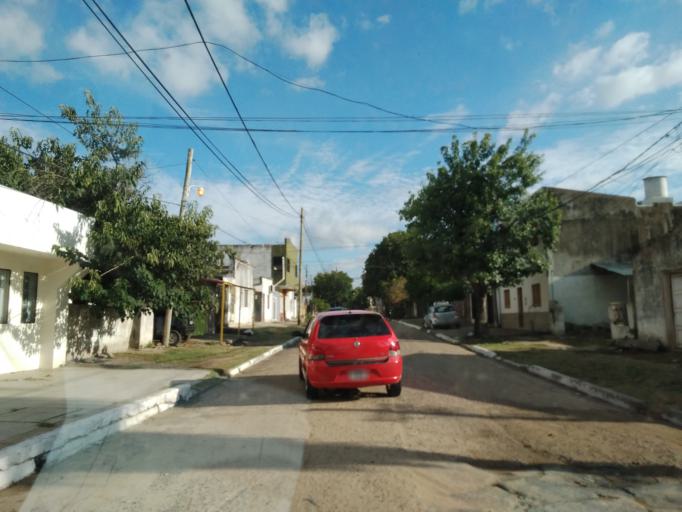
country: AR
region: Corrientes
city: Corrientes
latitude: -27.4599
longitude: -58.8191
